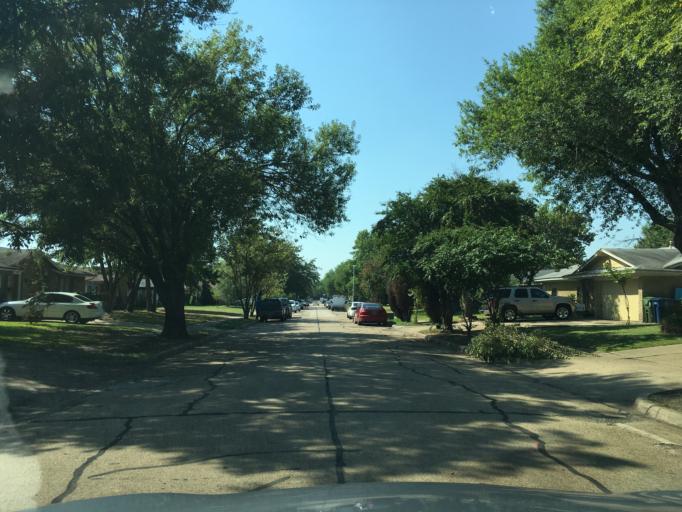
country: US
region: Texas
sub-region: Dallas County
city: Garland
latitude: 32.9329
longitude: -96.6327
